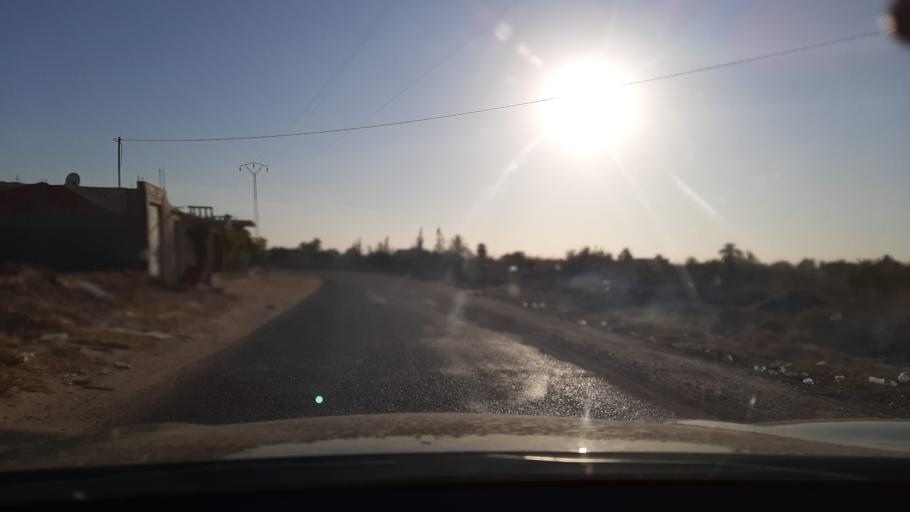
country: TN
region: Qabis
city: Matmata
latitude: 33.6194
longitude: 10.2703
